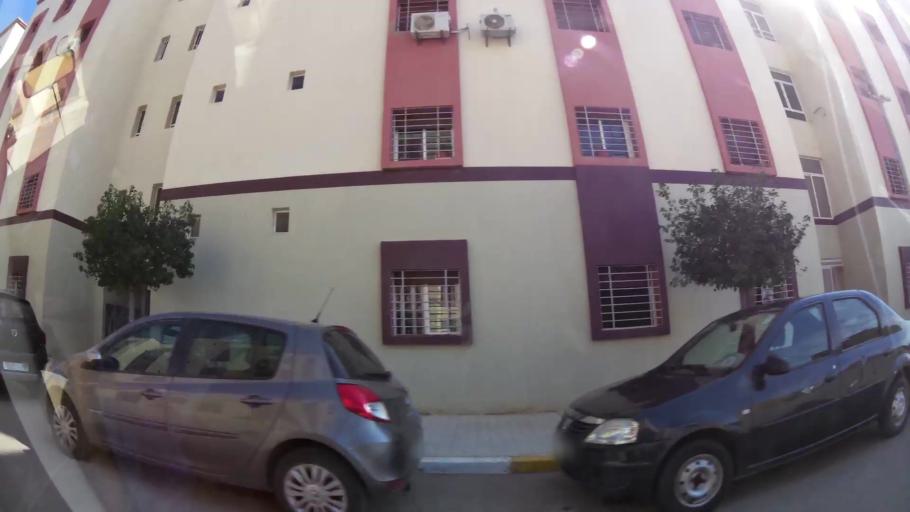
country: MA
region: Oriental
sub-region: Oujda-Angad
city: Oujda
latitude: 34.6993
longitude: -1.8751
